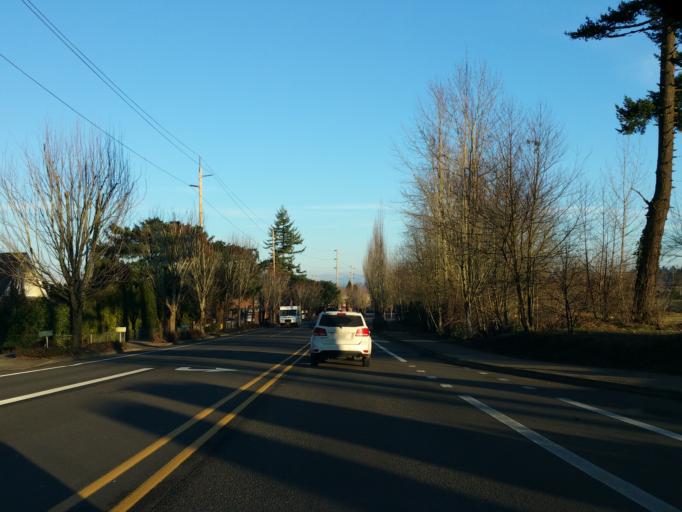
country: US
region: Oregon
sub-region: Multnomah County
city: Fairview
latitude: 45.5342
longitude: -122.4395
